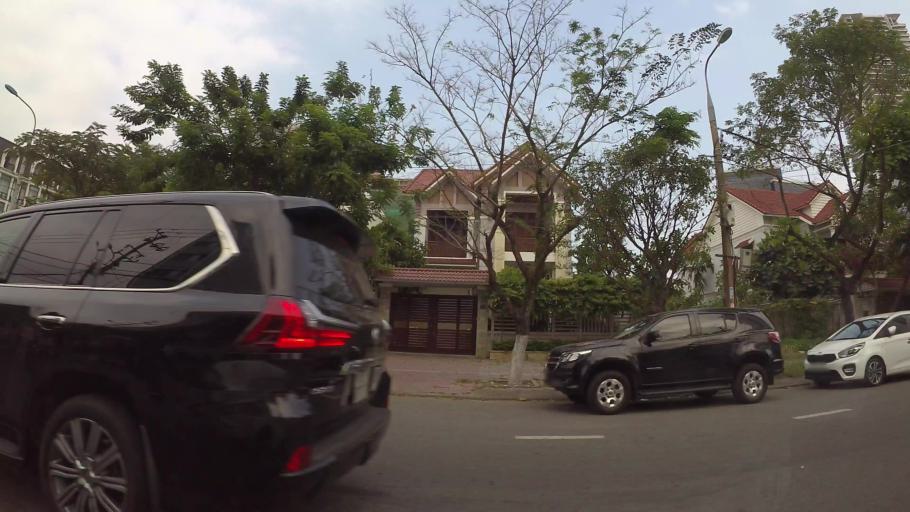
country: VN
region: Da Nang
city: Son Tra
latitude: 16.0732
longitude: 108.2430
